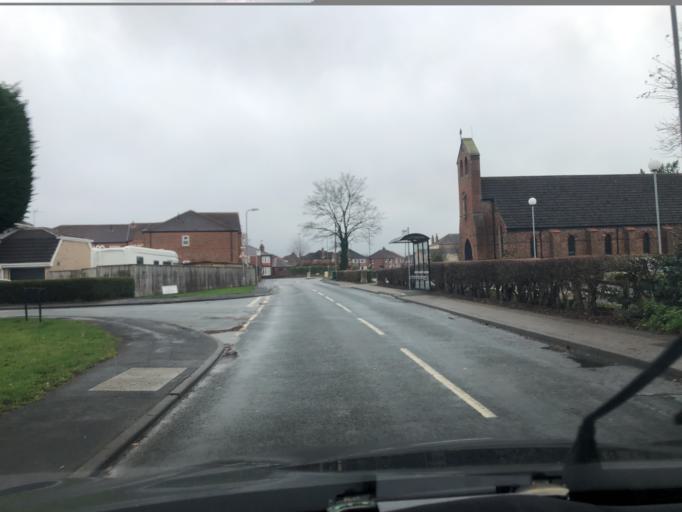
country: GB
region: England
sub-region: North Yorkshire
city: Stokesley
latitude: 54.4758
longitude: -1.1870
